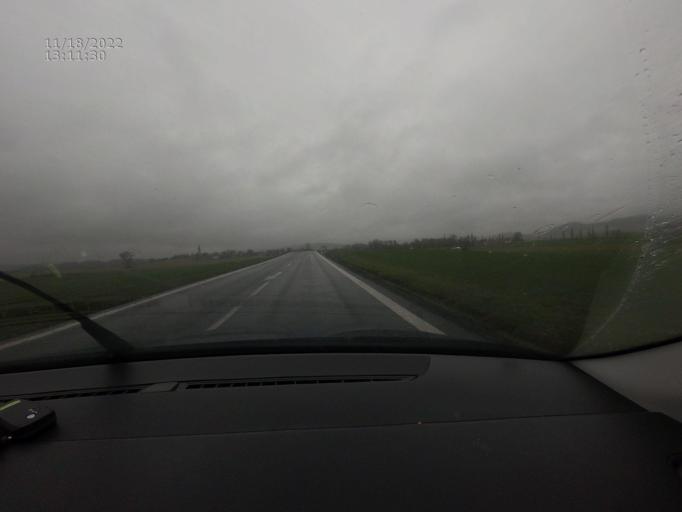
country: CZ
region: Plzensky
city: Hradek
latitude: 49.3267
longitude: 13.5866
